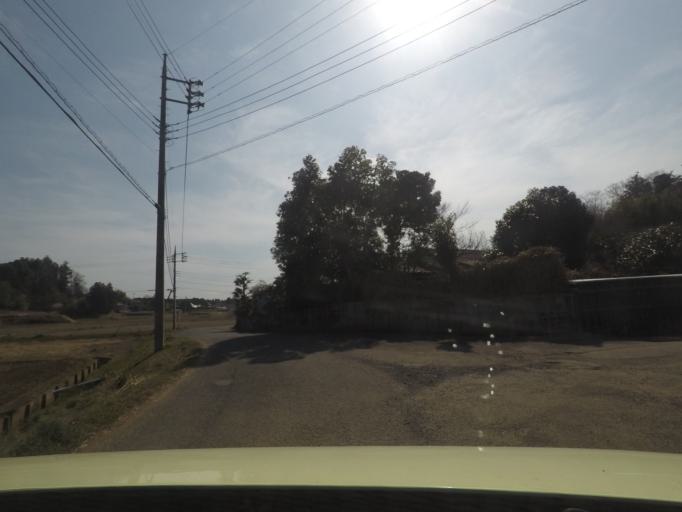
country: JP
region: Ibaraki
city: Ishioka
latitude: 36.1784
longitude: 140.3718
